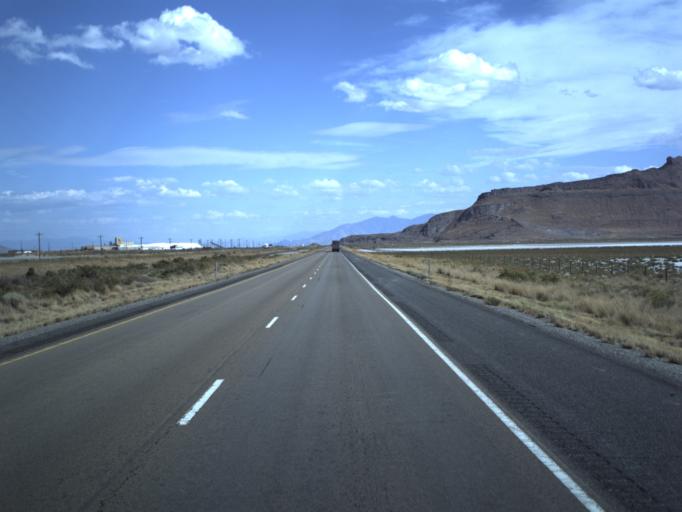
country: US
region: Utah
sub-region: Tooele County
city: Grantsville
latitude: 40.7485
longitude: -112.6819
